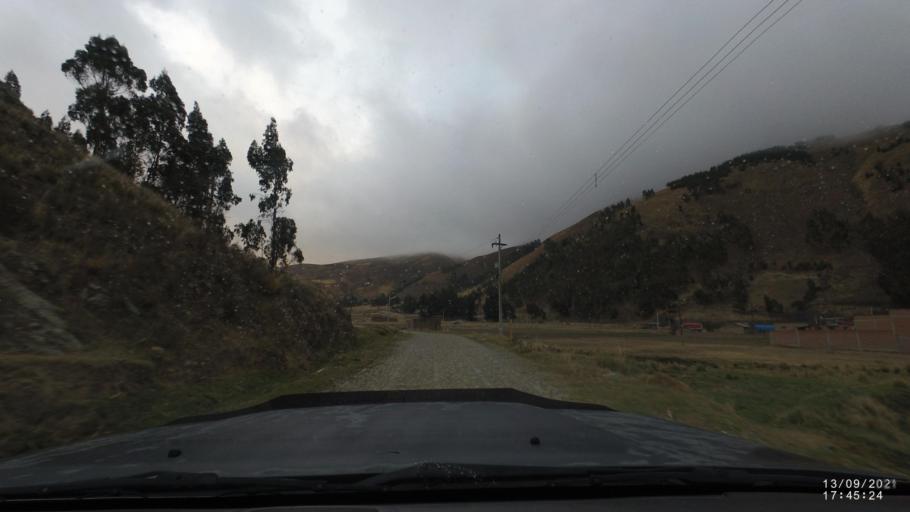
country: BO
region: Cochabamba
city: Colomi
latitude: -17.3775
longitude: -65.8325
